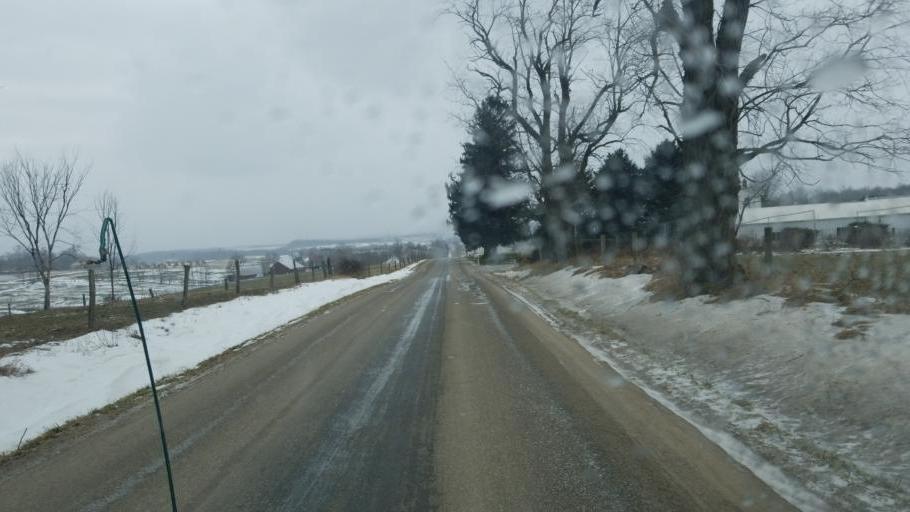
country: US
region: Ohio
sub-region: Wayne County
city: Apple Creek
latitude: 40.6752
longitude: -81.7884
